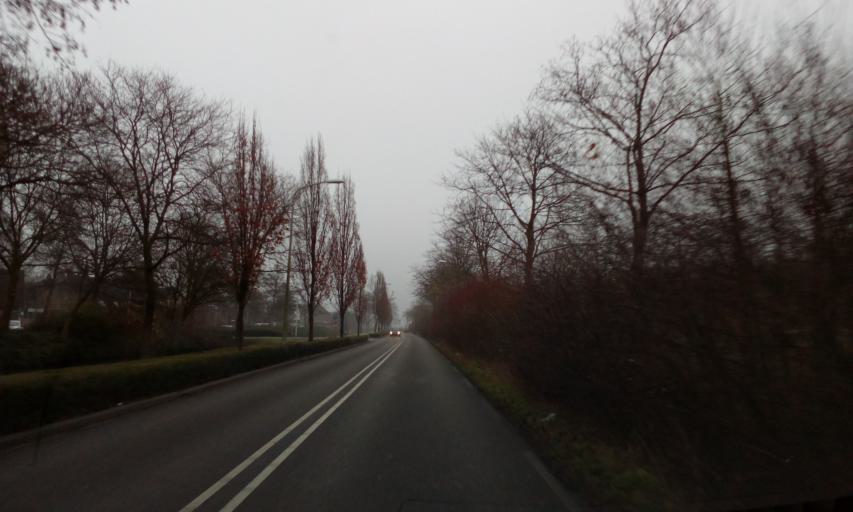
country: NL
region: South Holland
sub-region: Gemeente Krimpen aan den IJssel
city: Krimpen aan den IJssel
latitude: 51.9694
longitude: 4.6214
